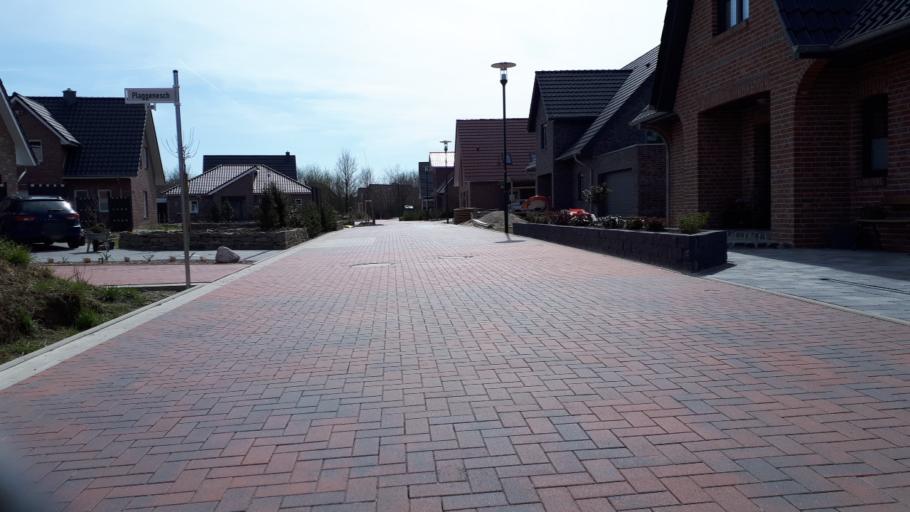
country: DE
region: Lower Saxony
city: Wardenburg
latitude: 53.0710
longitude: 8.1959
